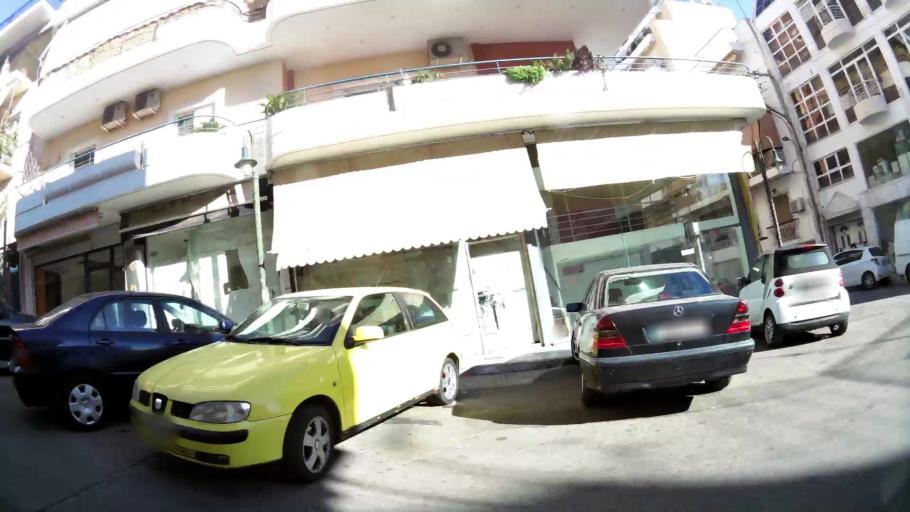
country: GR
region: Attica
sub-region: Nomos Piraios
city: Perama
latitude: 37.9644
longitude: 23.5710
